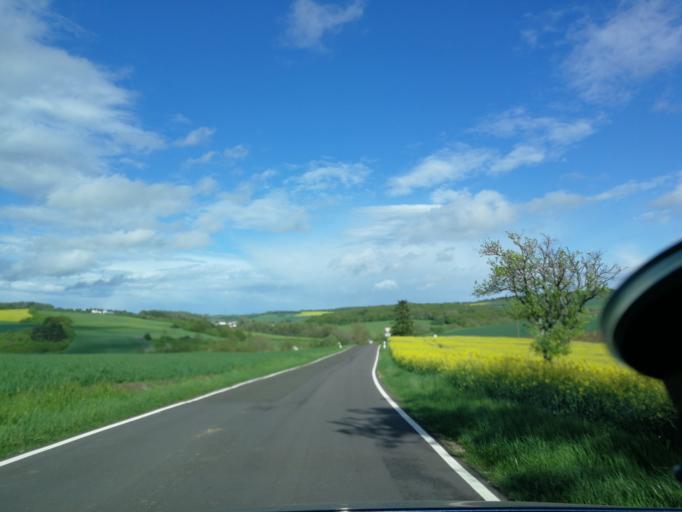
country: DE
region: Rheinland-Pfalz
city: Trierweiler
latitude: 49.7543
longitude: 6.5310
